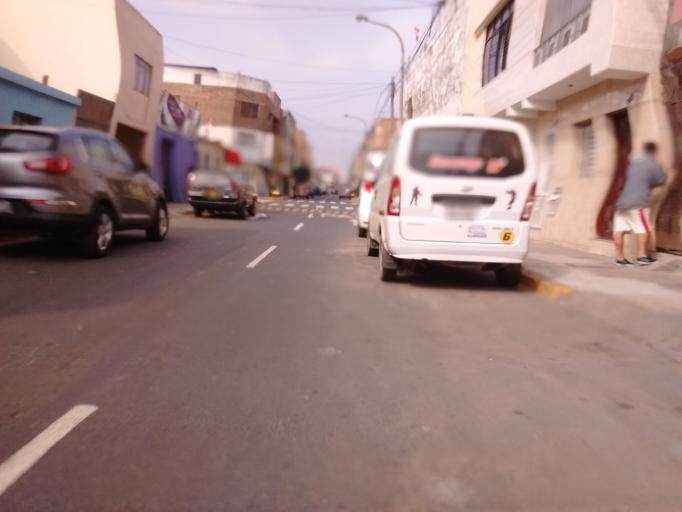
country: PE
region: Callao
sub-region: Callao
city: Callao
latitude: -12.0405
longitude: -77.0922
